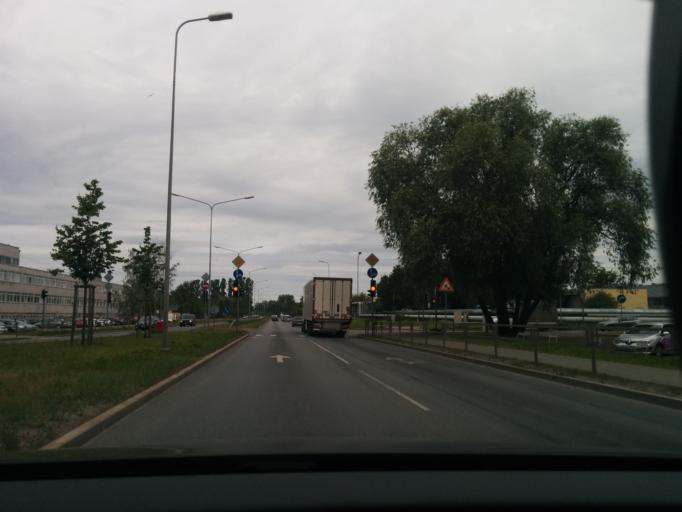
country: LV
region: Kekava
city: Balozi
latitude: 56.9200
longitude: 24.1943
